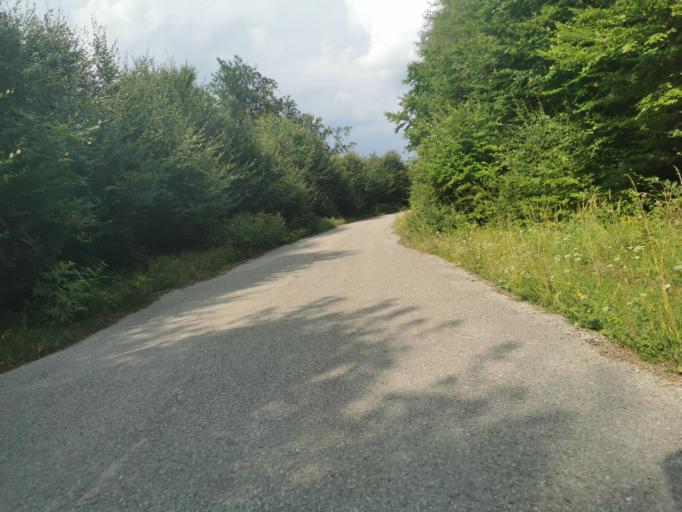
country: SK
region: Nitriansky
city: Stara Tura
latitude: 48.8118
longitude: 17.6292
